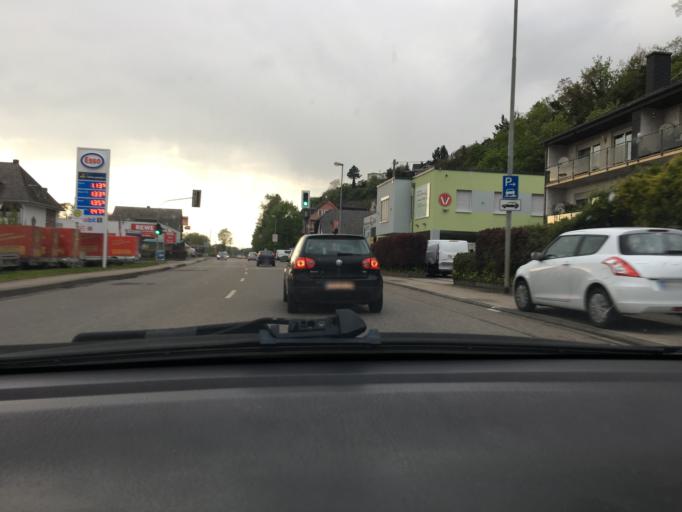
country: DE
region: Rheinland-Pfalz
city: Niederwerth
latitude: 50.4018
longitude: 7.6082
